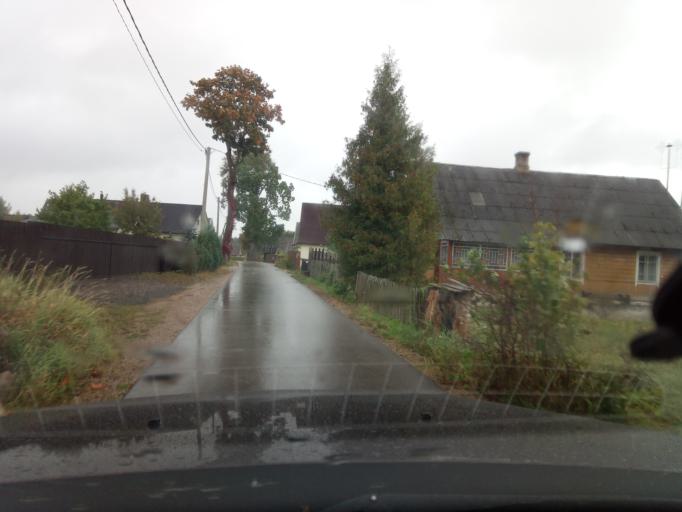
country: LT
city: Skaidiskes
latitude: 54.5981
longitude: 25.5827
